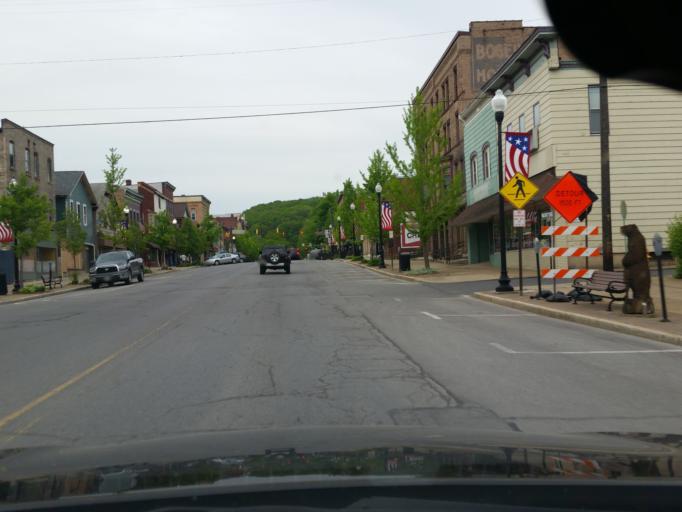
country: US
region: Pennsylvania
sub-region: Elk County
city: Ridgway
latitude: 41.4209
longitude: -78.7326
